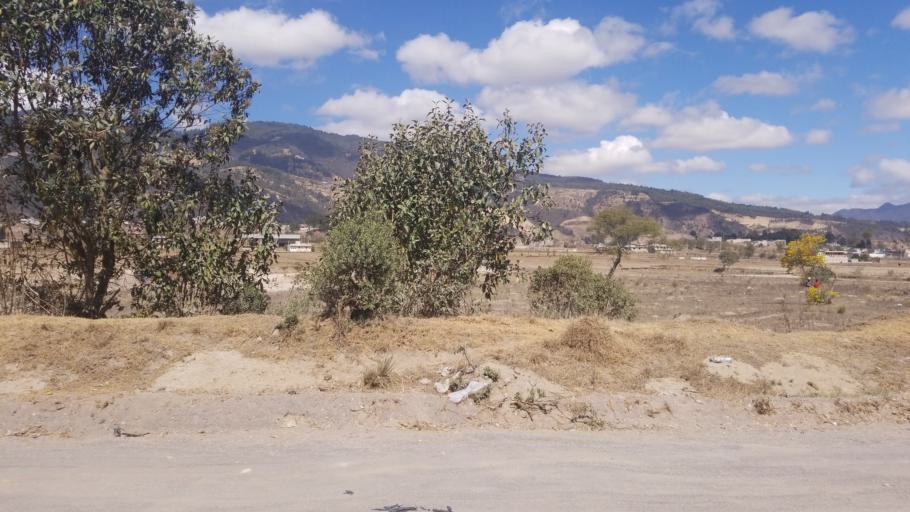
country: GT
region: Quetzaltenango
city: Quetzaltenango
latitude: 14.8025
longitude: -91.5376
